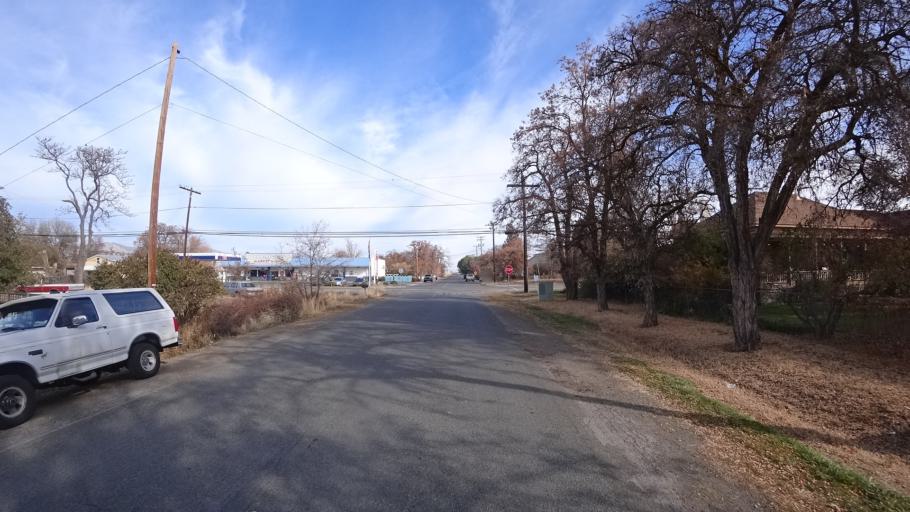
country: US
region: California
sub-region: Siskiyou County
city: Montague
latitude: 41.7266
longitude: -122.5249
